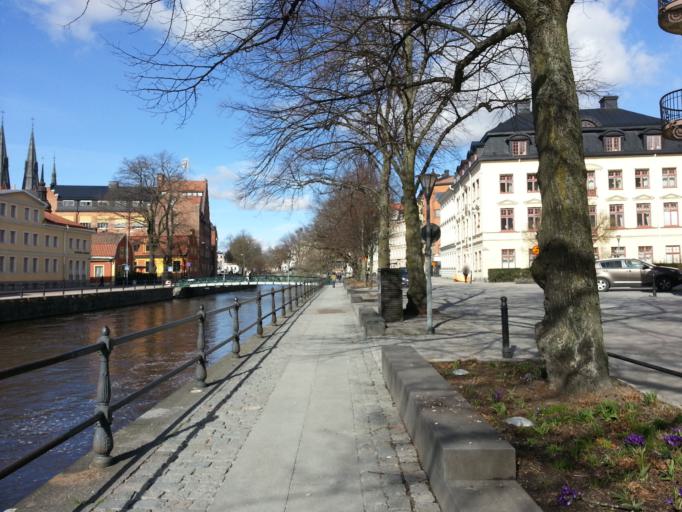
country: SE
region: Uppsala
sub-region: Uppsala Kommun
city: Uppsala
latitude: 59.8561
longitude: 17.6405
